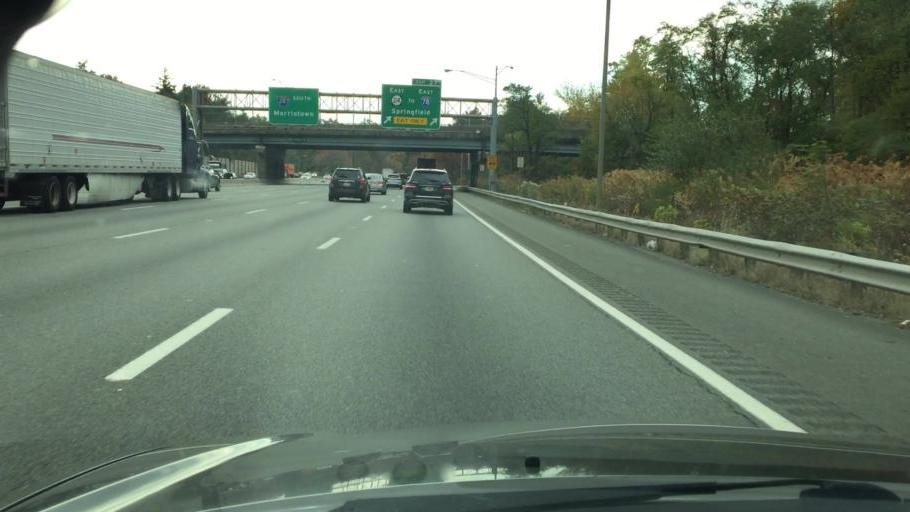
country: US
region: New Jersey
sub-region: Morris County
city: Morris Plains
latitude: 40.8167
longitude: -74.4449
